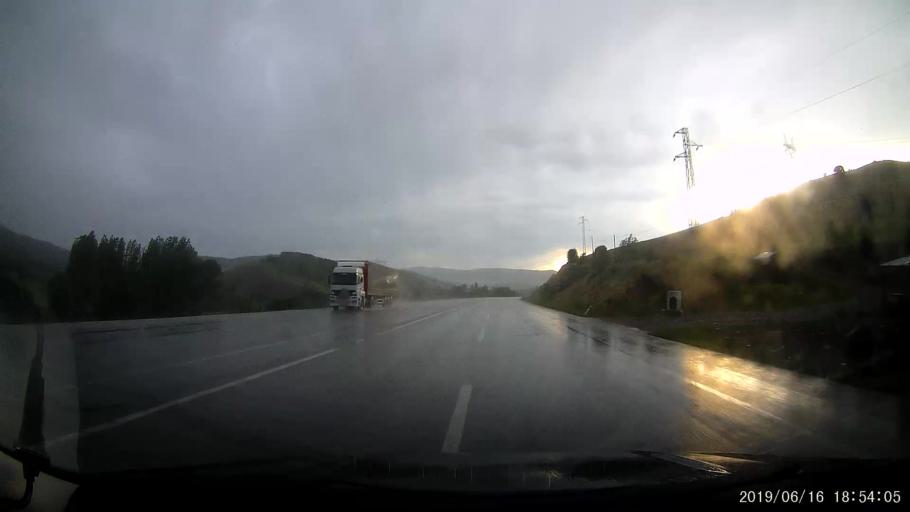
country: TR
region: Erzincan
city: Catalcam
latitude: 39.8964
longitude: 38.8617
